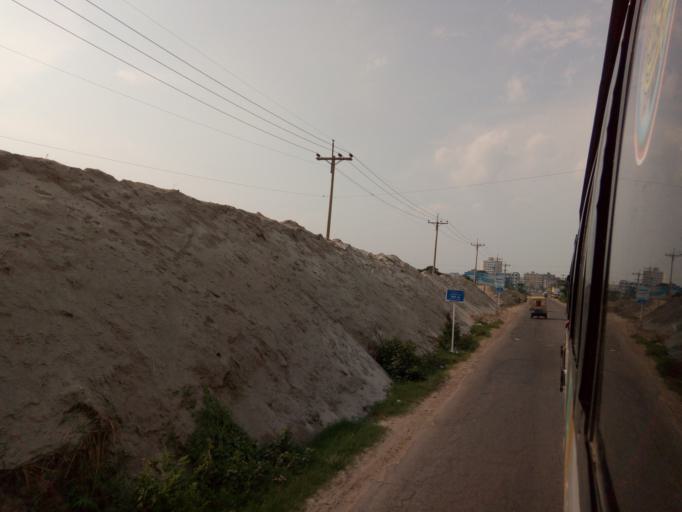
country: BD
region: Dhaka
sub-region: Dhaka
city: Dhaka
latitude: 23.6831
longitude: 90.4030
